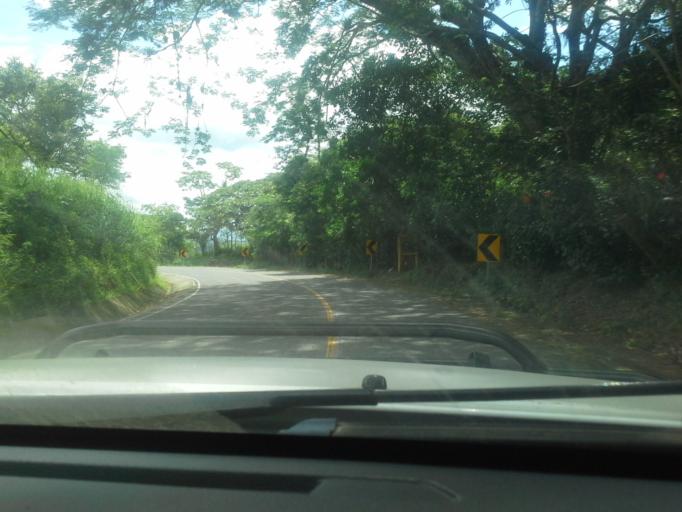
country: NI
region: Boaco
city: San Jose de los Remates
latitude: 12.6898
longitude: -85.7506
